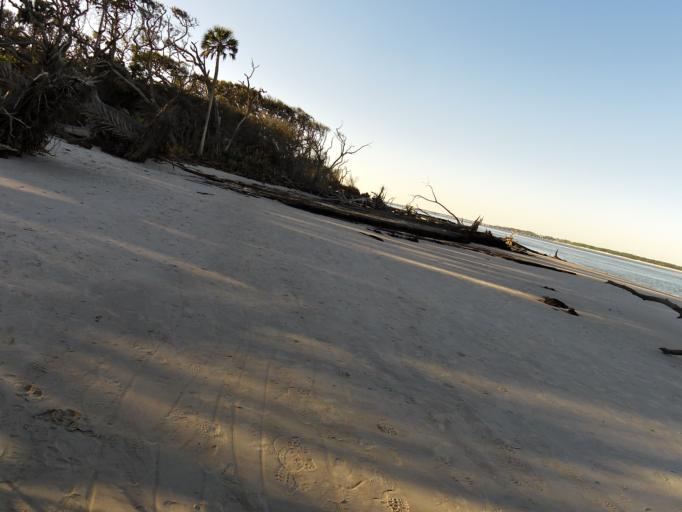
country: US
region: Florida
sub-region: Duval County
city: Atlantic Beach
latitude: 30.4925
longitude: -81.4388
